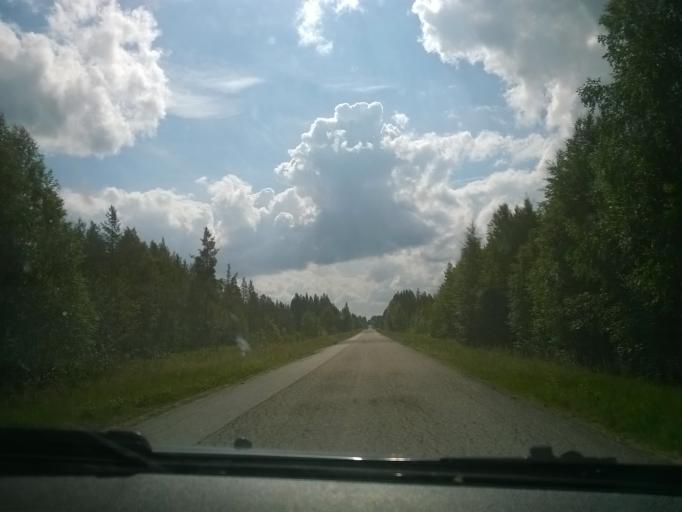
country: FI
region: Kainuu
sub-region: Kehys-Kainuu
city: Kuhmo
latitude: 64.4081
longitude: 29.7707
